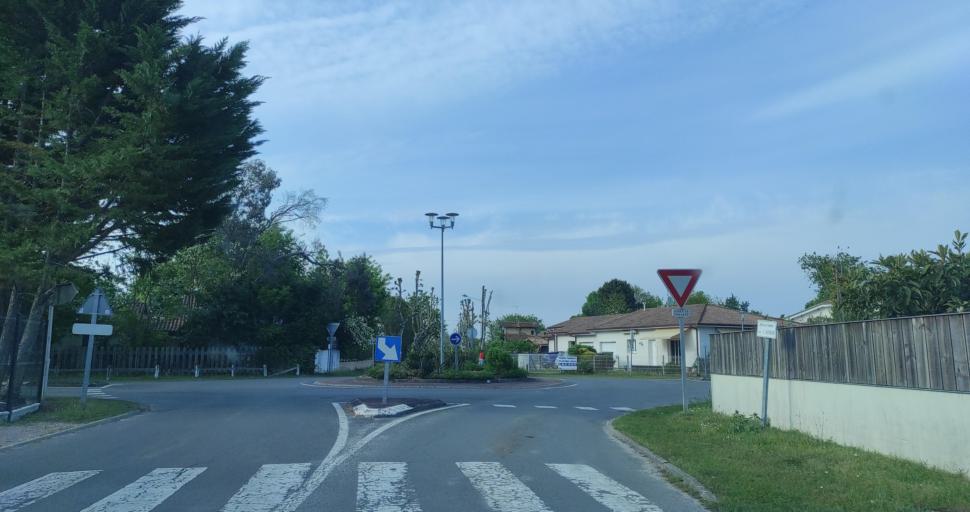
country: FR
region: Aquitaine
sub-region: Departement de la Gironde
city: Ares
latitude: 44.7605
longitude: -1.1327
